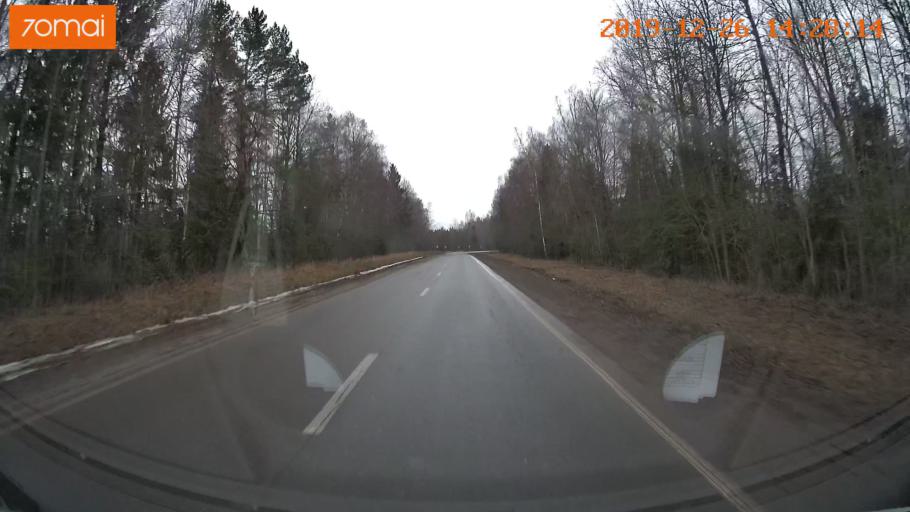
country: RU
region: Jaroslavl
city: Poshekhon'ye
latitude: 58.4773
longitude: 39.0556
